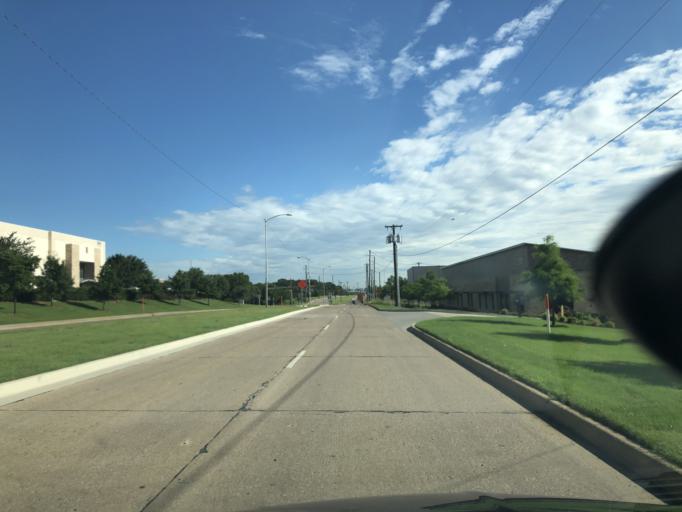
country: US
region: Texas
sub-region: Tarrant County
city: Euless
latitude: 32.8144
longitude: -97.0304
